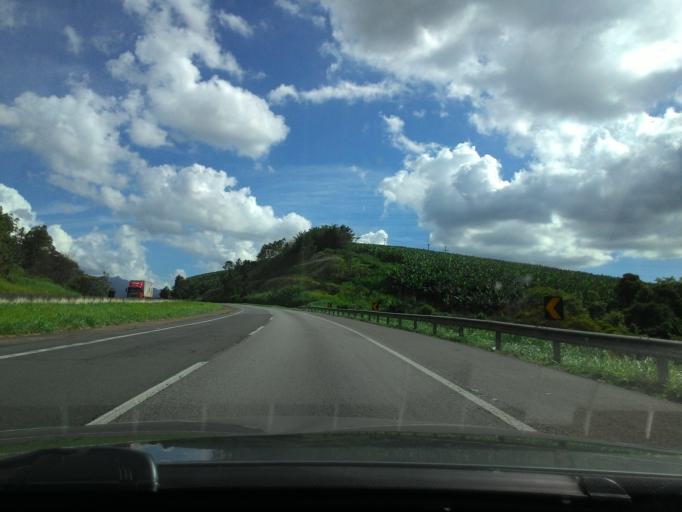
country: BR
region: Sao Paulo
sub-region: Cajati
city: Cajati
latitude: -24.7588
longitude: -48.1645
